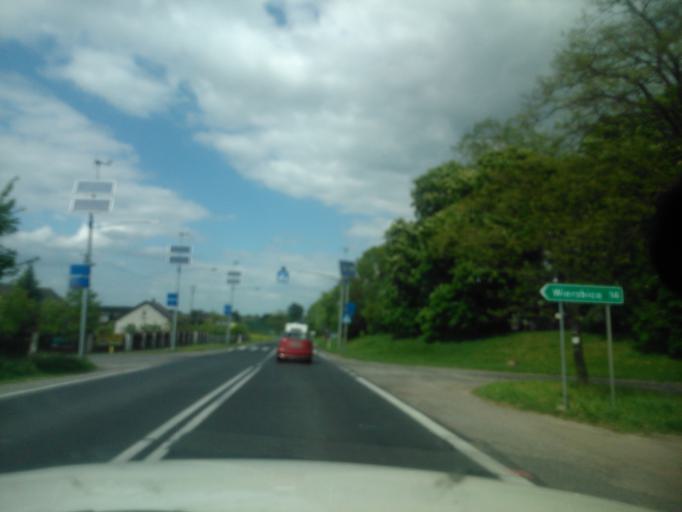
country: PL
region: Masovian Voivodeship
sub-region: Powiat radomski
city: Ilza
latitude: 51.1927
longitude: 21.2377
